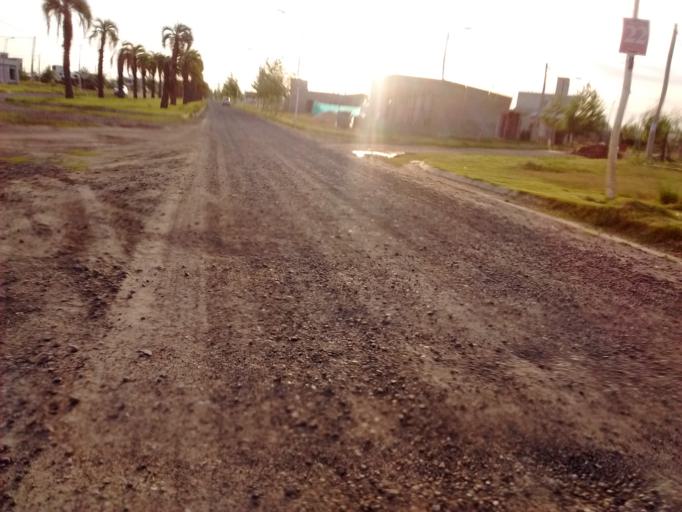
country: AR
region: Santa Fe
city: Roldan
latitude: -32.9366
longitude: -60.8786
